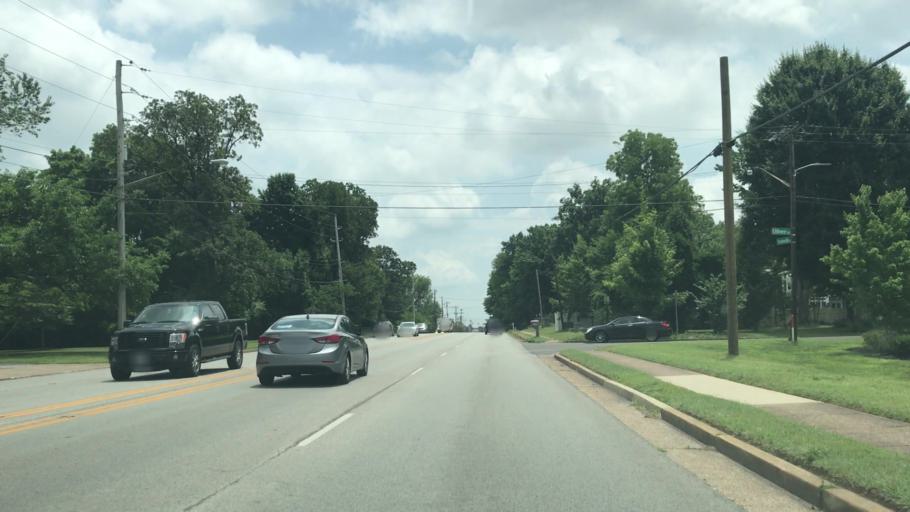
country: US
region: Kentucky
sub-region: Warren County
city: Bowling Green
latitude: 36.9747
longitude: -86.4364
